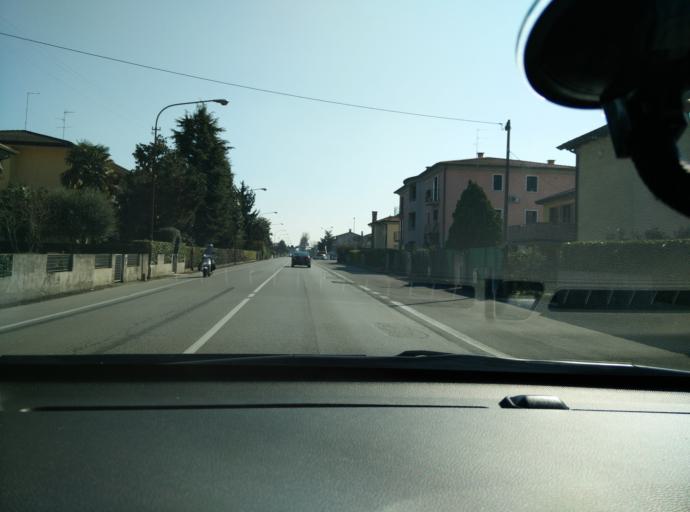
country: IT
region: Veneto
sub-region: Provincia di Venezia
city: Noventa di Piave
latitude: 45.6554
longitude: 12.5366
